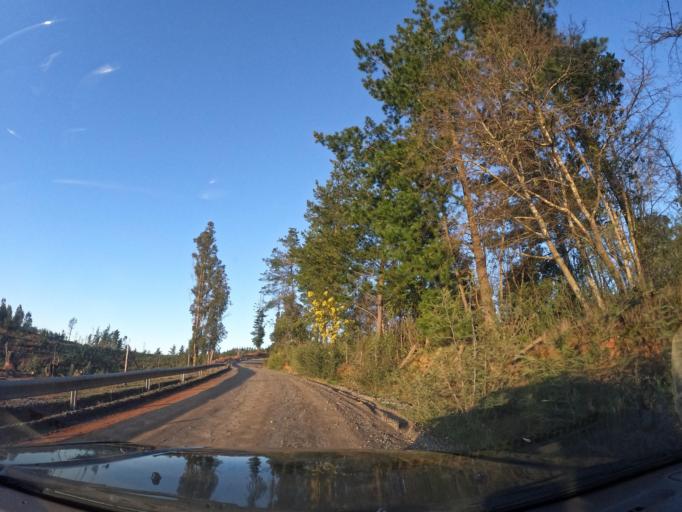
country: CL
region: Biobio
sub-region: Provincia de Concepcion
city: Chiguayante
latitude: -37.0099
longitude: -72.8914
